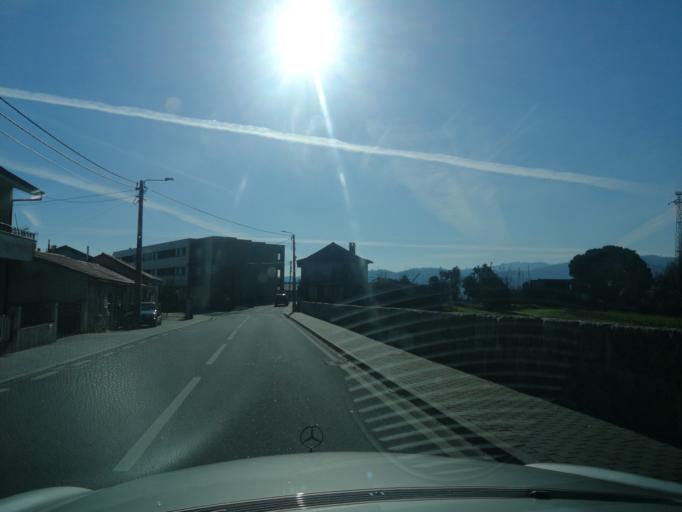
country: PT
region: Braga
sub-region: Guimaraes
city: Ponte
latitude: 41.4905
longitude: -8.3527
